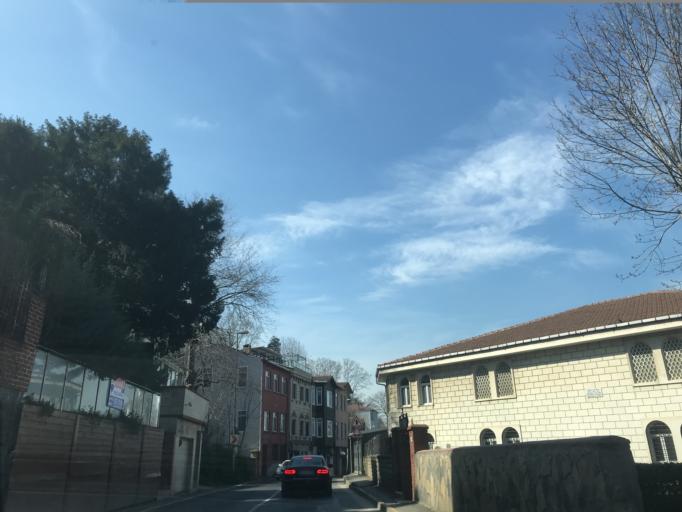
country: TR
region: Istanbul
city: Umraniye
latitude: 41.1071
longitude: 29.0832
